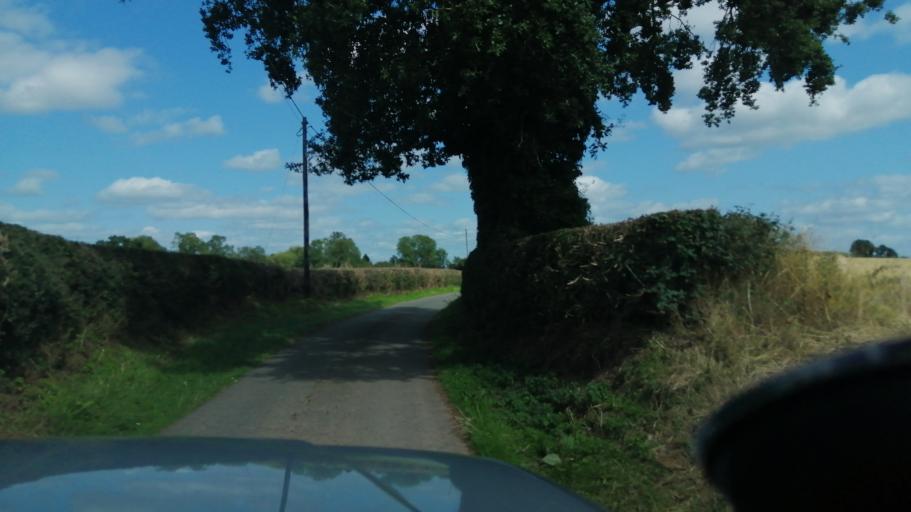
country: GB
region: England
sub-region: Herefordshire
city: Thruxton
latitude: 52.0096
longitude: -2.8169
